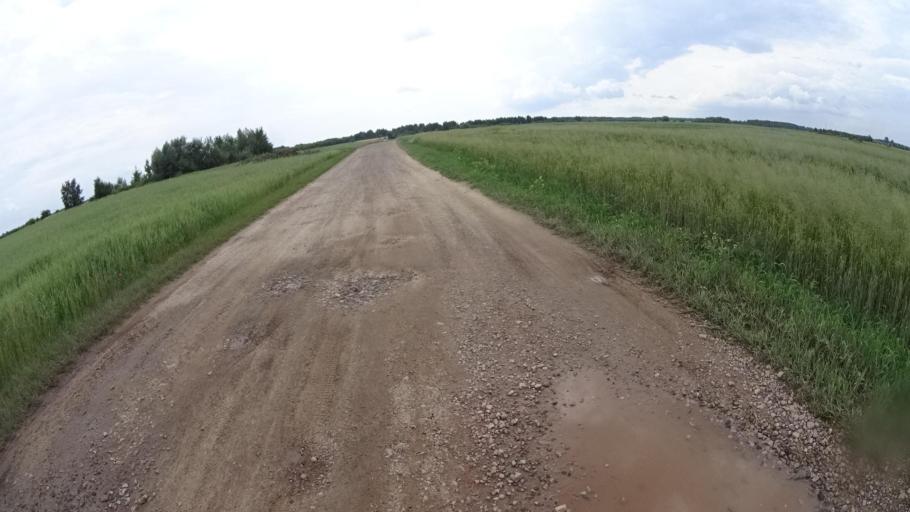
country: PL
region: Masovian Voivodeship
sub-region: Powiat piaseczynski
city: Tarczyn
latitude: 52.0256
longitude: 20.8178
